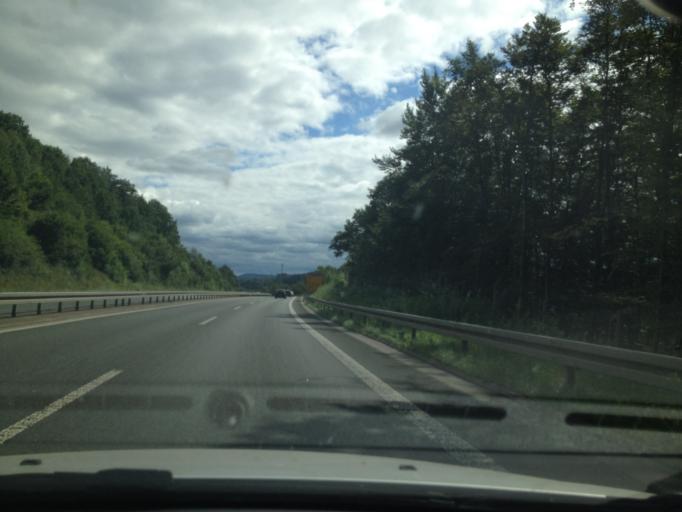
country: DE
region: North Rhine-Westphalia
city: Kreuztal
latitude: 50.9451
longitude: 8.0042
